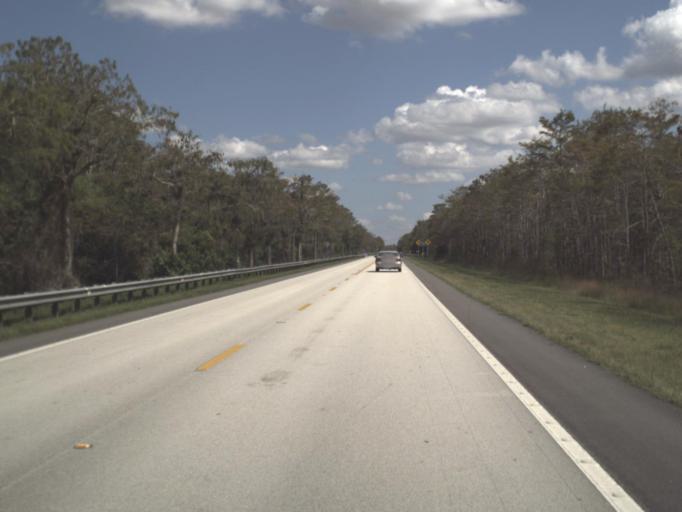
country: US
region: Florida
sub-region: Miami-Dade County
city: Kendall West
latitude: 25.8470
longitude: -80.9352
